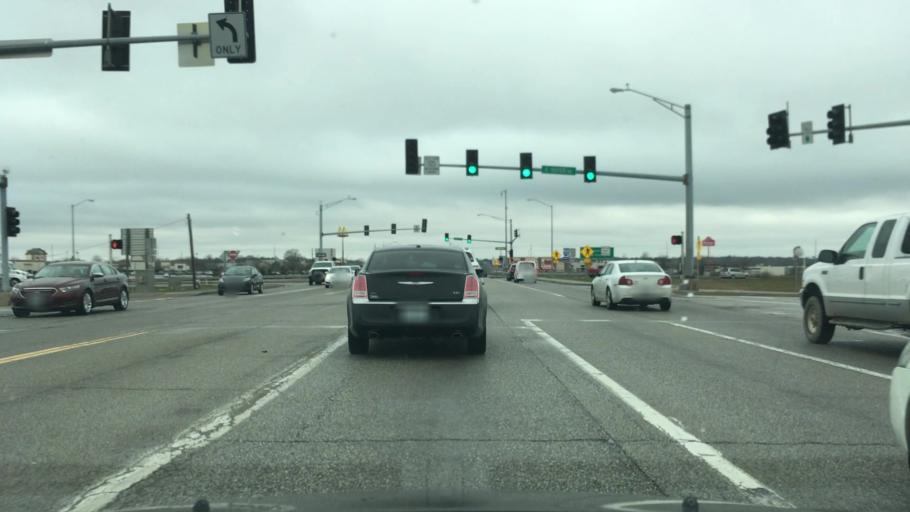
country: US
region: Missouri
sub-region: Cass County
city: Belton
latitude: 38.8132
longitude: -94.5014
